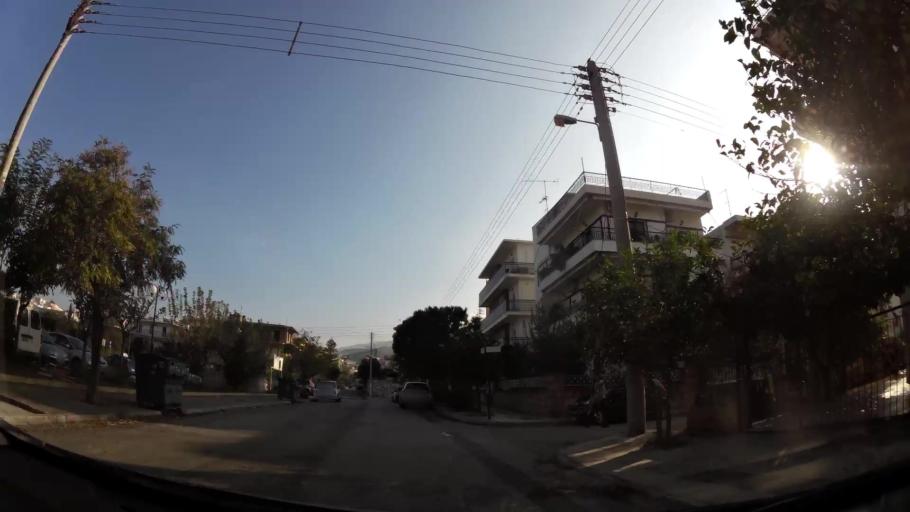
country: GR
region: Attica
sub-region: Nomarchia Athinas
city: Ilioupoli
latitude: 37.9340
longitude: 23.7530
